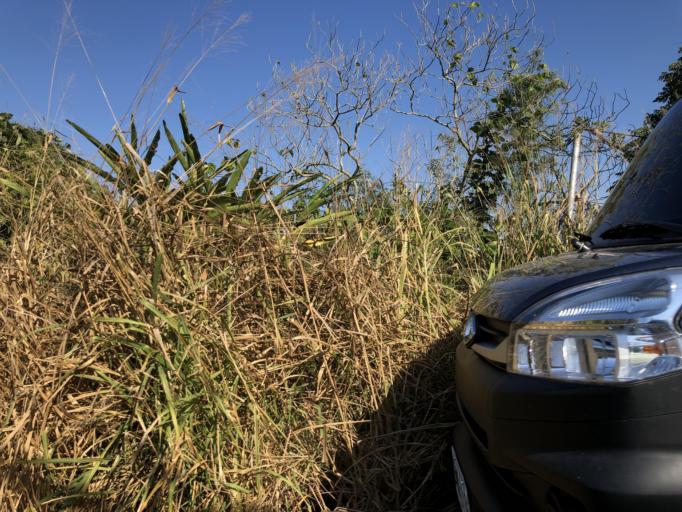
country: TW
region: Taiwan
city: Yujing
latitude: 23.0291
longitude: 120.3857
